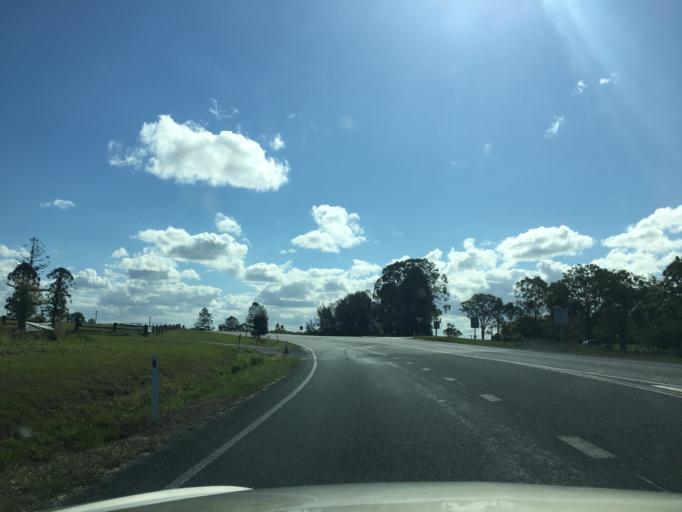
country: AU
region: Queensland
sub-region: Logan
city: Waterford West
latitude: -27.7079
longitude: 153.1351
